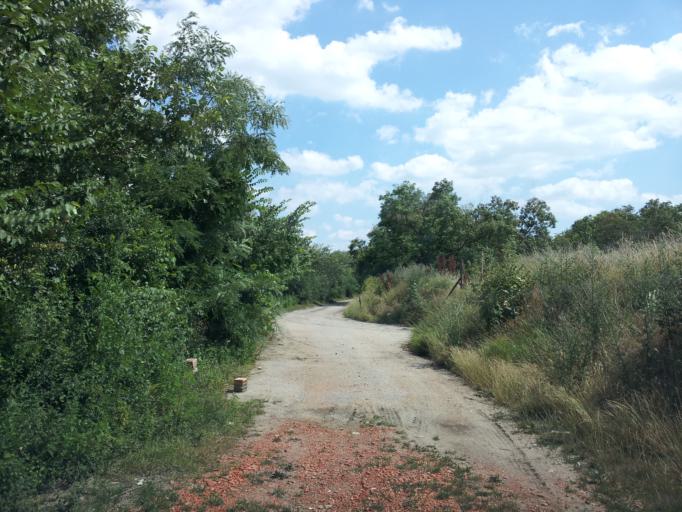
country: HU
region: Veszprem
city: Balatonkenese
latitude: 47.0534
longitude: 18.0692
